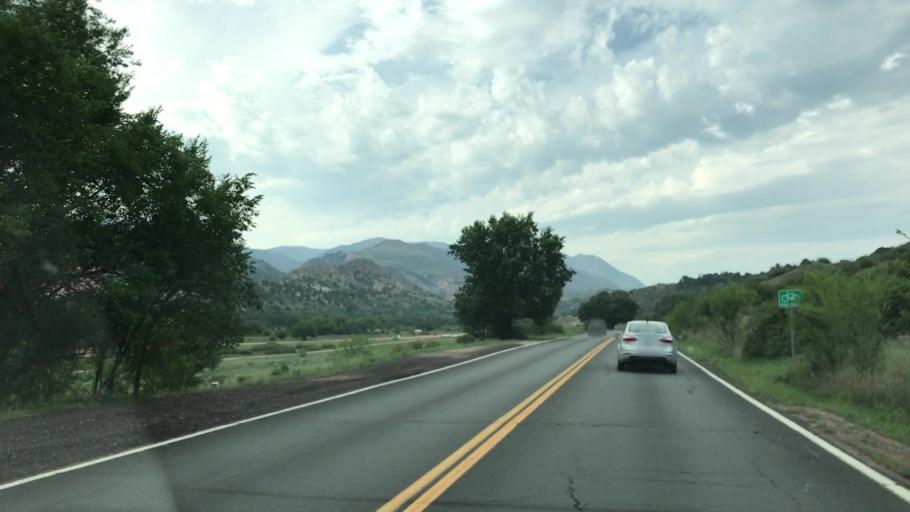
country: US
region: Colorado
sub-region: El Paso County
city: Manitou Springs
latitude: 38.8723
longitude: -104.8684
